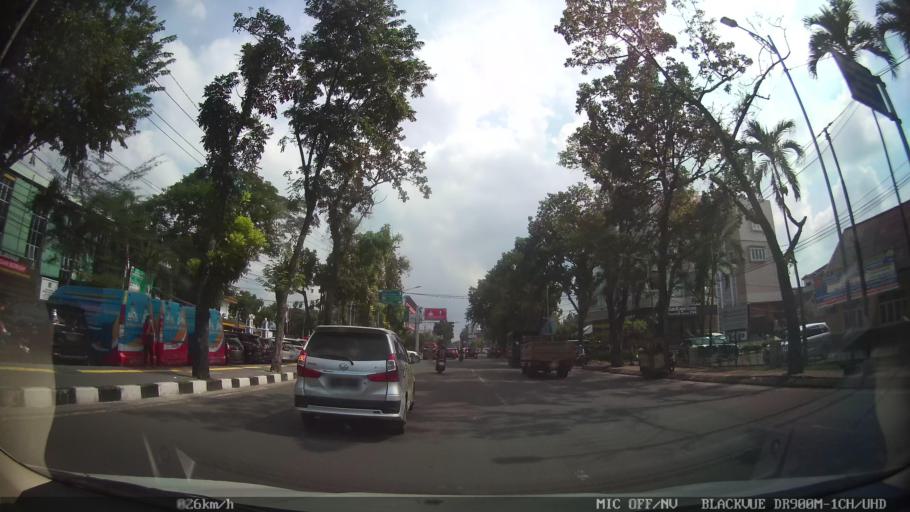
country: ID
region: North Sumatra
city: Medan
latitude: 3.5859
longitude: 98.6613
